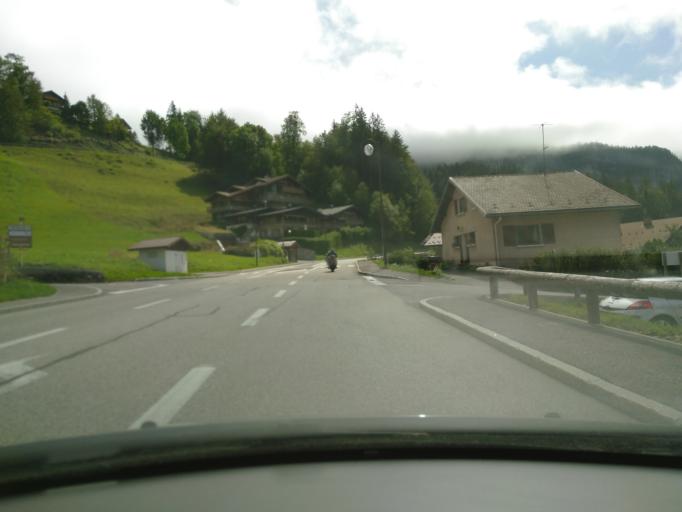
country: FR
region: Rhone-Alpes
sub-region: Departement de la Haute-Savoie
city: Saint-Jean-de-Sixt
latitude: 45.9233
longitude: 6.4133
